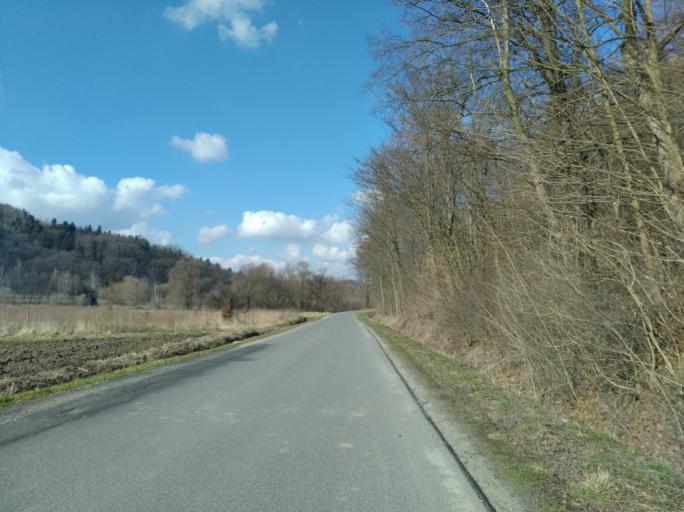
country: PL
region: Subcarpathian Voivodeship
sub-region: Powiat strzyzowski
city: Frysztak
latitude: 49.8506
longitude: 21.6245
